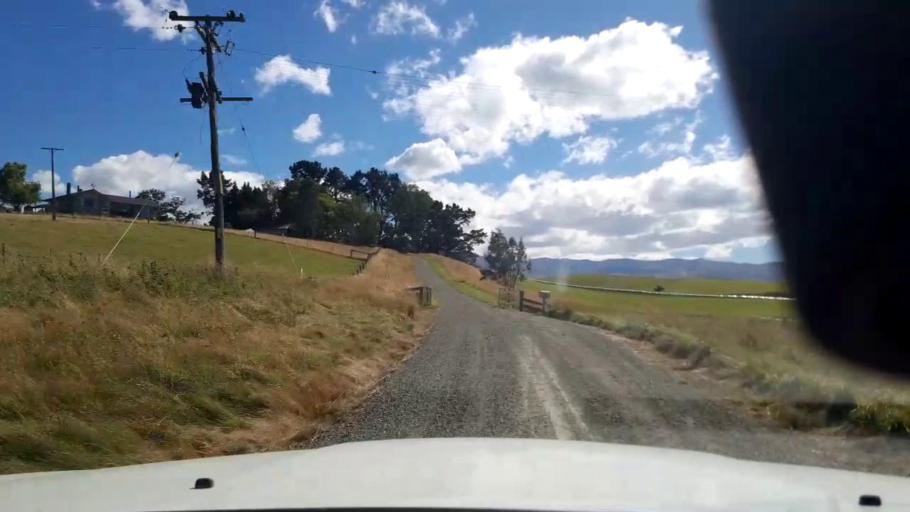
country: NZ
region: Canterbury
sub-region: Timaru District
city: Pleasant Point
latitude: -44.2404
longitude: 170.8581
